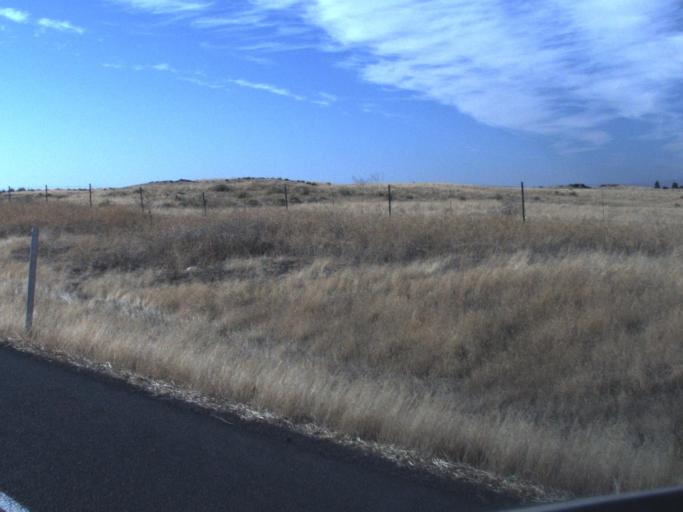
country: US
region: Washington
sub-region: Franklin County
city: Connell
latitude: 46.6406
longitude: -119.0064
